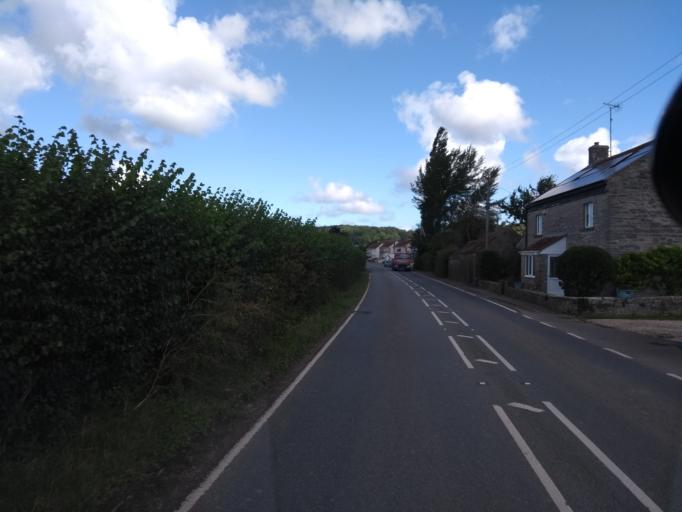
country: GB
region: England
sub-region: Somerset
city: Street
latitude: 51.0960
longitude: -2.7329
